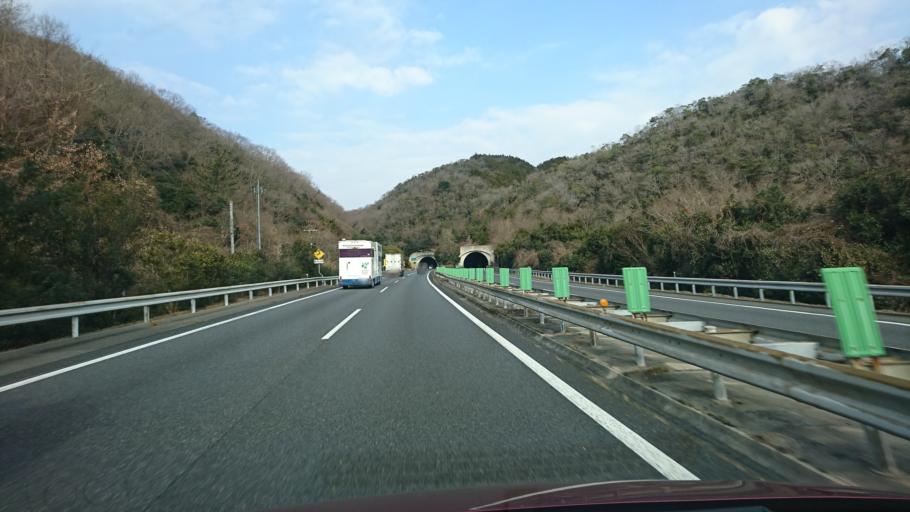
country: JP
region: Hyogo
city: Kariya
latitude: 34.7865
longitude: 134.2164
